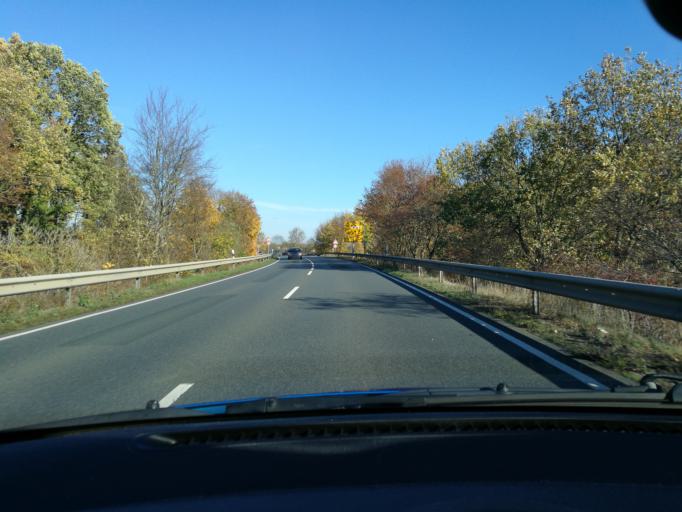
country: DE
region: Lower Saxony
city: Dannenberg
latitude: 53.0971
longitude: 11.1168
